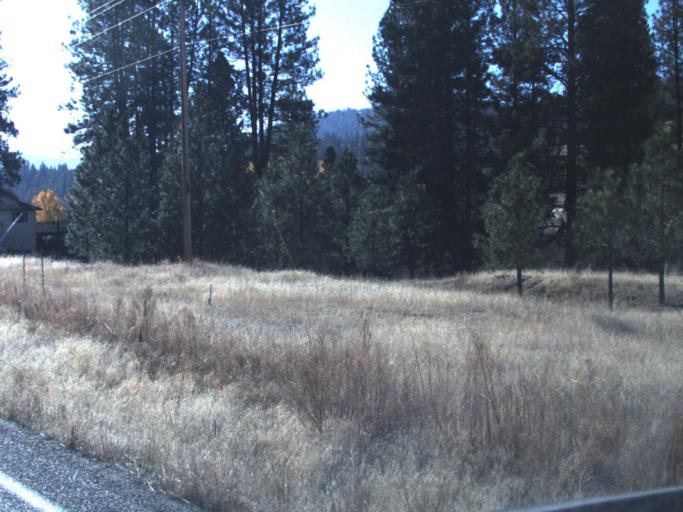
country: US
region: Washington
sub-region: Ferry County
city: Republic
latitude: 48.8502
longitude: -118.6005
